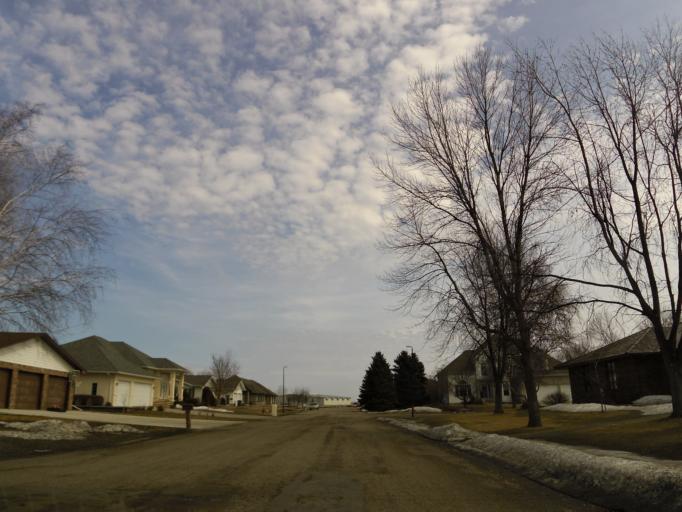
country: US
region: North Dakota
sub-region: Walsh County
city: Grafton
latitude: 48.4047
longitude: -97.4153
